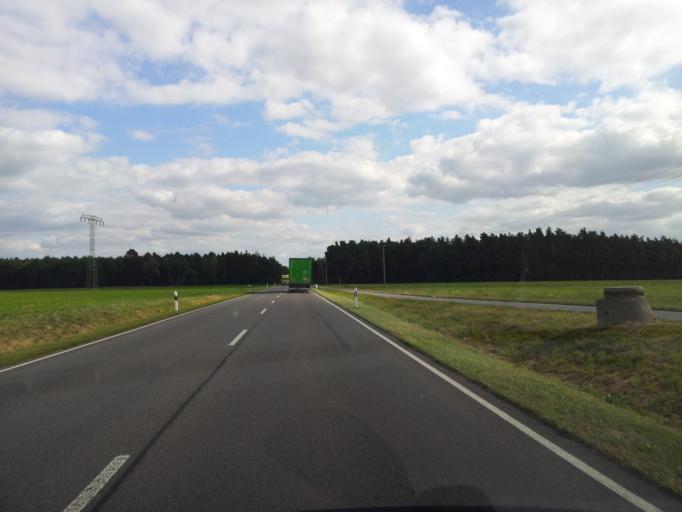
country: DE
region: Brandenburg
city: Sallgast
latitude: 51.6141
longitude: 13.8367
